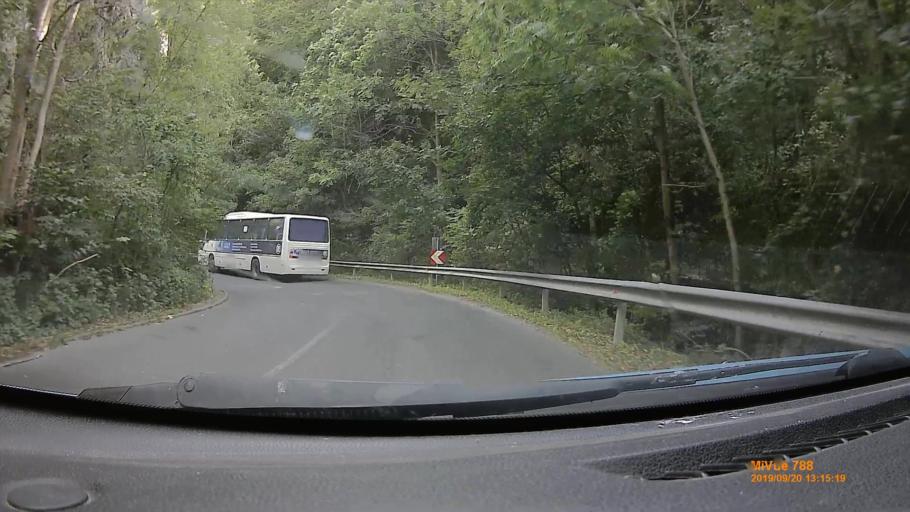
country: HU
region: Heves
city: Felsotarkany
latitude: 47.9826
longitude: 20.4378
